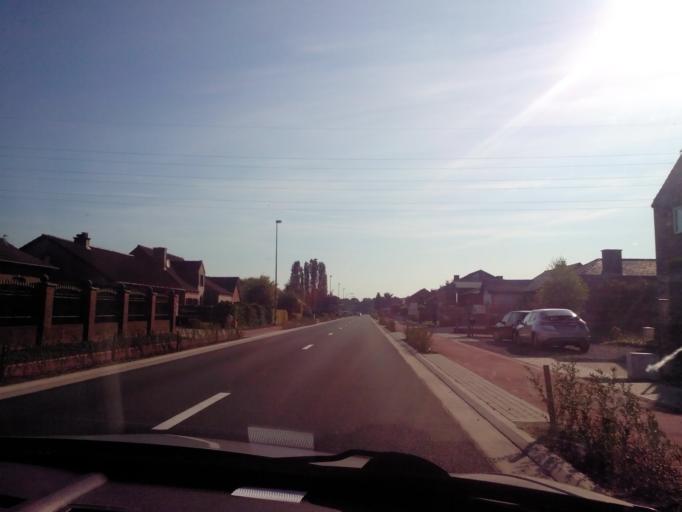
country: BE
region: Flanders
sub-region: Provincie Limburg
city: Opglabbeek
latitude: 51.0345
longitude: 5.5540
